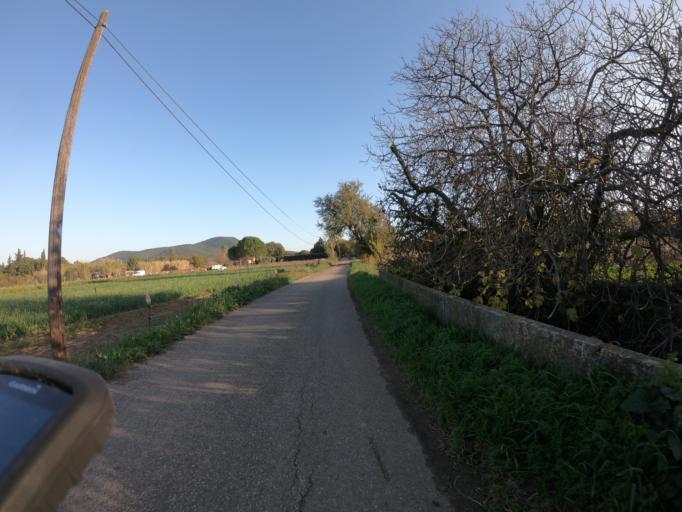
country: FR
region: Provence-Alpes-Cote d'Azur
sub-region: Departement du Var
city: Le Pradet
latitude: 43.1137
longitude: 6.0373
